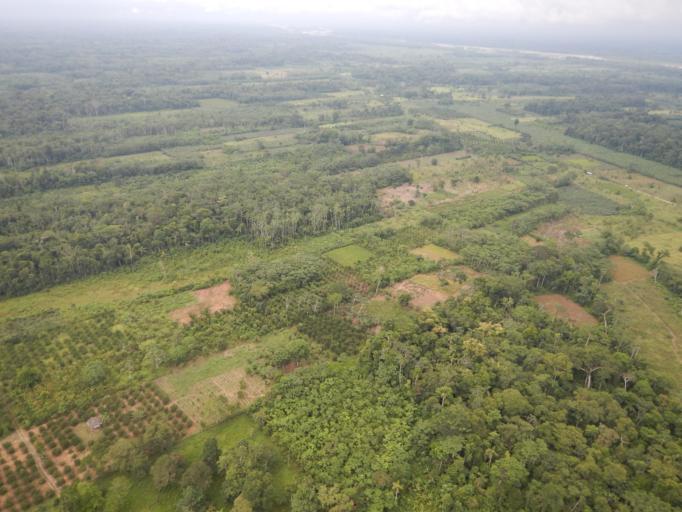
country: BO
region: Cochabamba
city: Chimore
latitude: -17.1332
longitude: -64.7830
